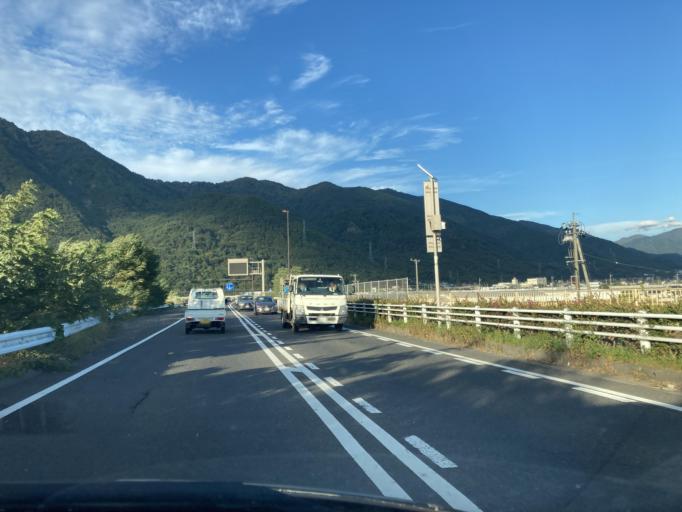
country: JP
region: Nagano
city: Ueda
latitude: 36.4110
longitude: 138.2175
